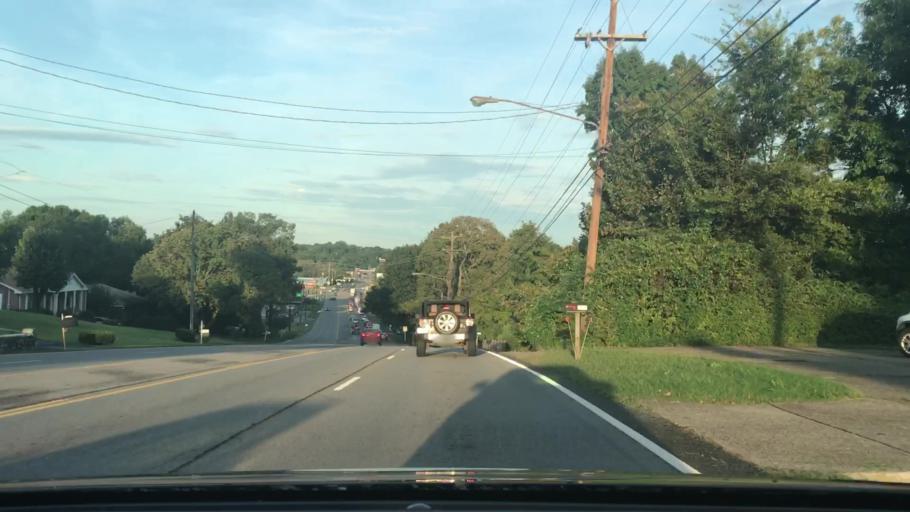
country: US
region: Tennessee
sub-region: Davidson County
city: Oak Hill
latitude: 36.0773
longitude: -86.7331
